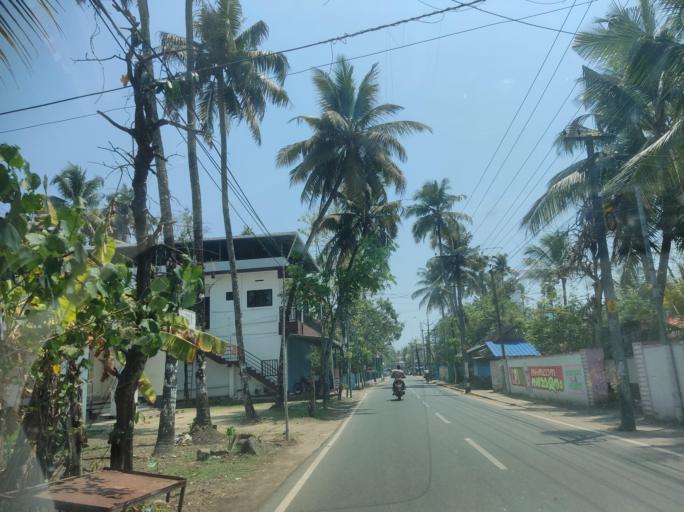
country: IN
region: Kerala
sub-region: Ernakulam
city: Cochin
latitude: 9.8948
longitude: 76.2844
